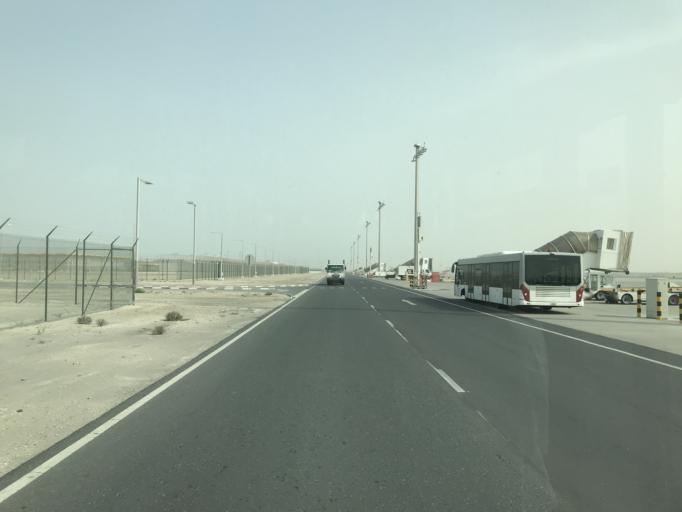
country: QA
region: Baladiyat ad Dawhah
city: Doha
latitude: 25.2762
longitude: 51.6001
